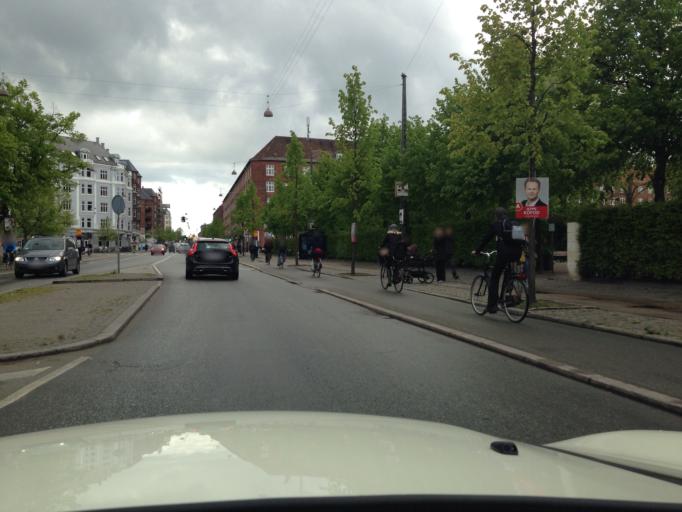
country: DK
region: Capital Region
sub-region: Frederiksberg Kommune
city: Frederiksberg
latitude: 55.6670
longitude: 12.5439
